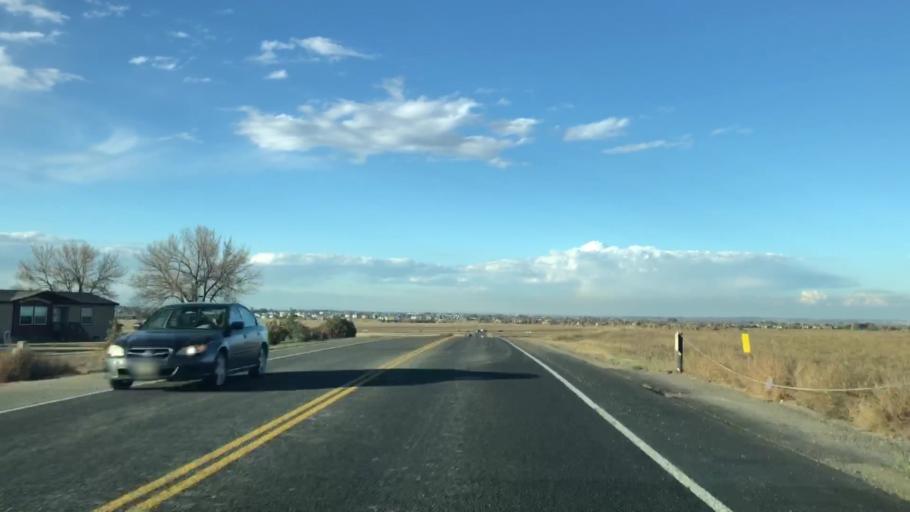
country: US
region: Colorado
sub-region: Larimer County
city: Loveland
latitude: 40.4729
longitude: -105.0202
